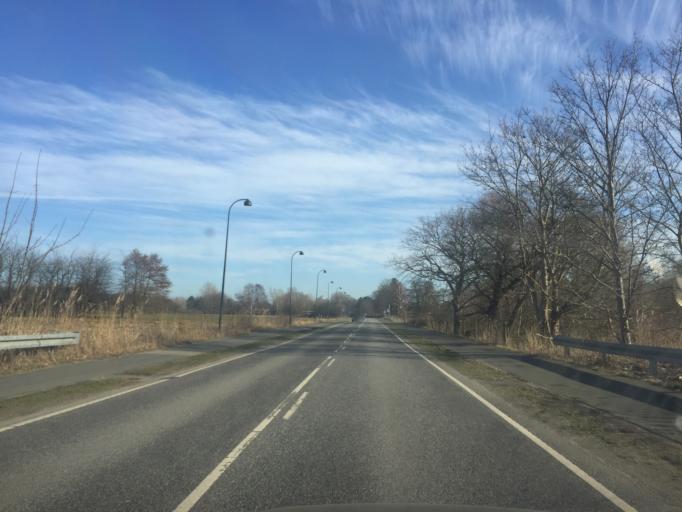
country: DK
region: Capital Region
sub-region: Rudersdal Kommune
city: Trorod
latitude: 55.8504
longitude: 12.5538
